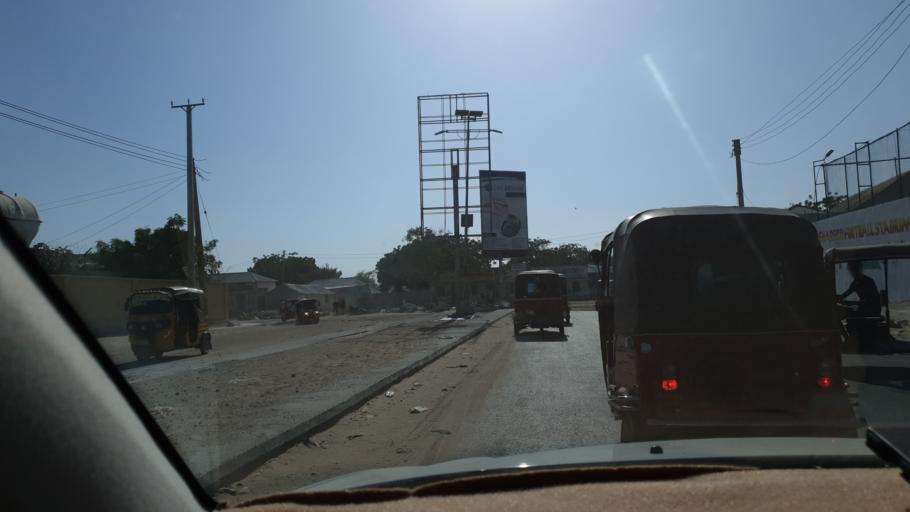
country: SO
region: Banaadir
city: Mogadishu
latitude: 2.0514
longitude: 45.3097
